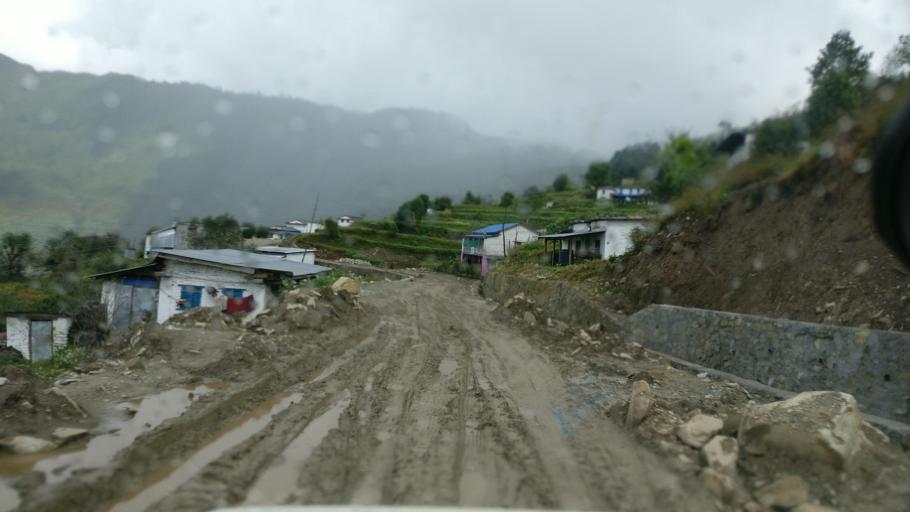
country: NP
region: Western Region
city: Baglung
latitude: 28.2831
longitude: 83.6422
